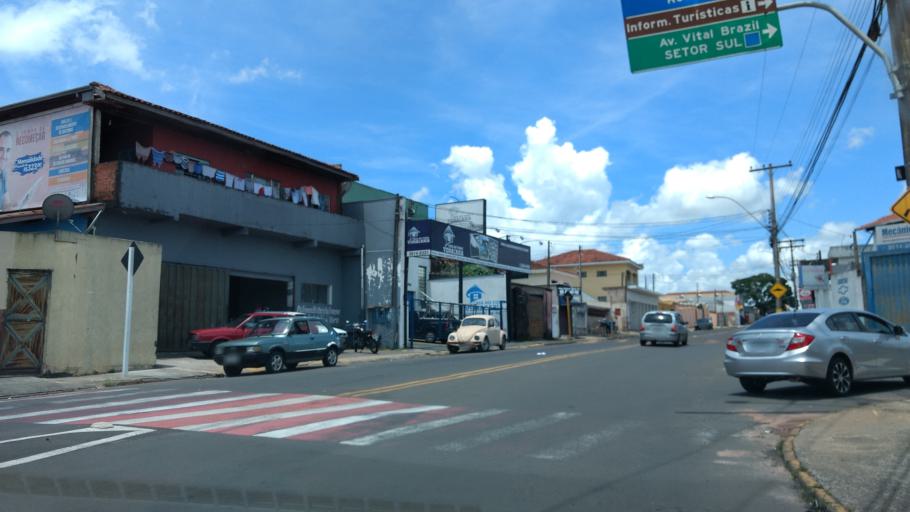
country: BR
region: Sao Paulo
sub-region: Botucatu
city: Botucatu
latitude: -22.8693
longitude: -48.4602
